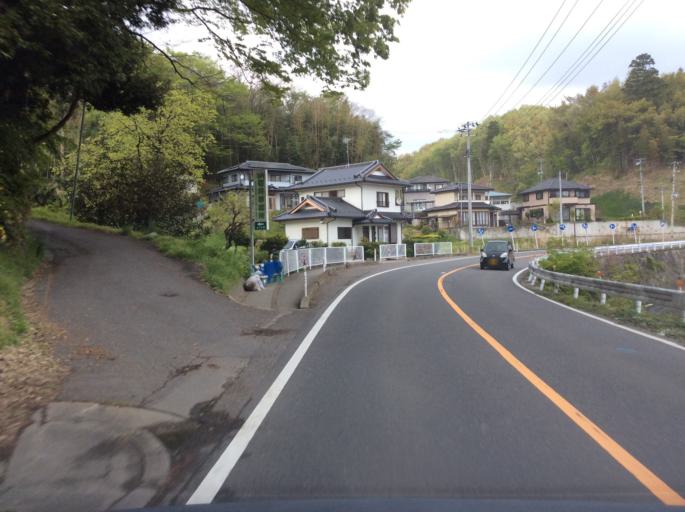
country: JP
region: Fukushima
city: Miharu
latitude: 37.4185
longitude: 140.4352
